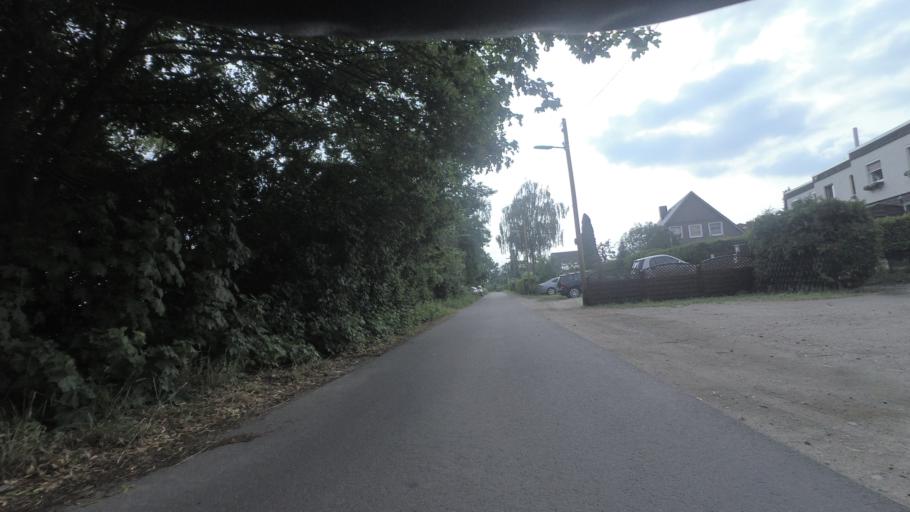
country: DE
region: Berlin
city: Gropiusstadt
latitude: 52.4200
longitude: 13.4563
